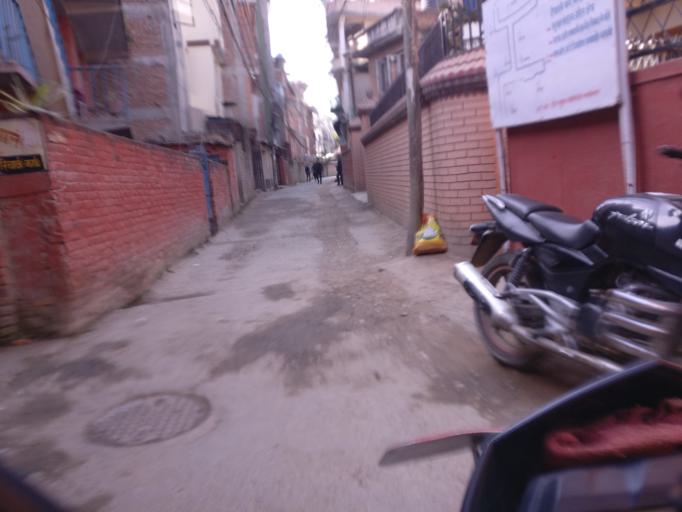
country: NP
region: Central Region
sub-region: Bagmati Zone
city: Patan
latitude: 27.6601
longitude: 85.3259
